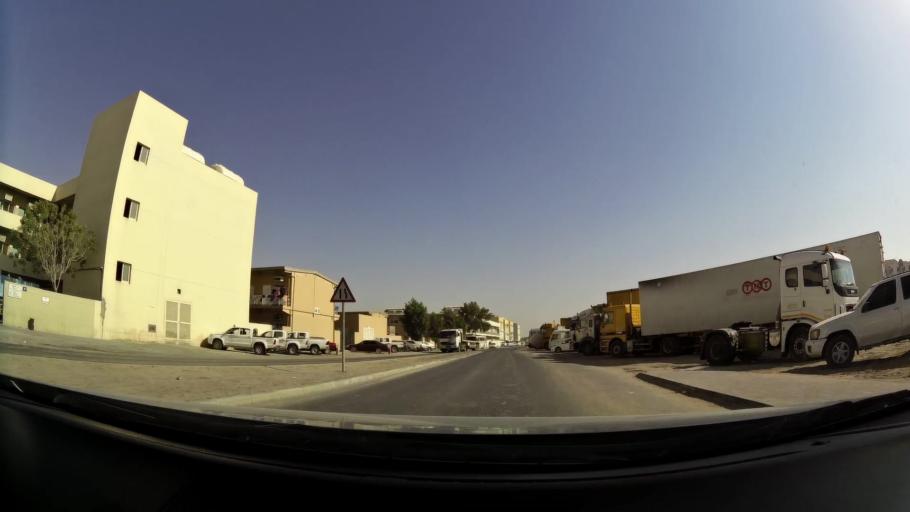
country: AE
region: Dubai
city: Dubai
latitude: 25.0030
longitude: 55.1061
